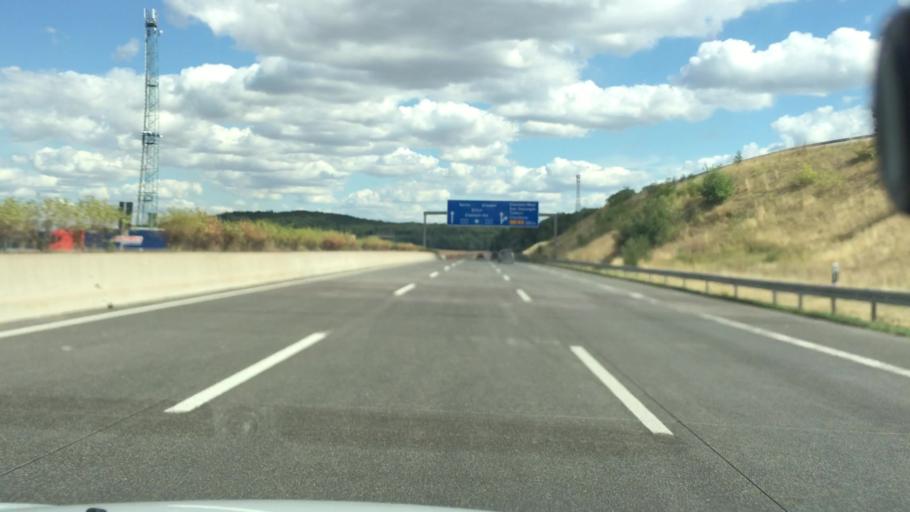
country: DE
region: Thuringia
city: Krauthausen
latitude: 51.0066
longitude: 10.2535
